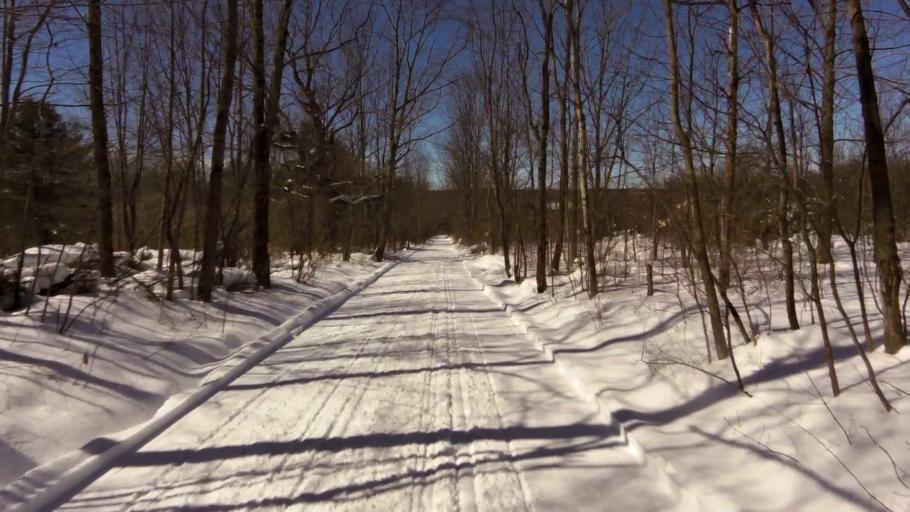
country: US
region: New York
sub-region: Allegany County
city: Cuba
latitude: 42.3267
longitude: -78.2405
